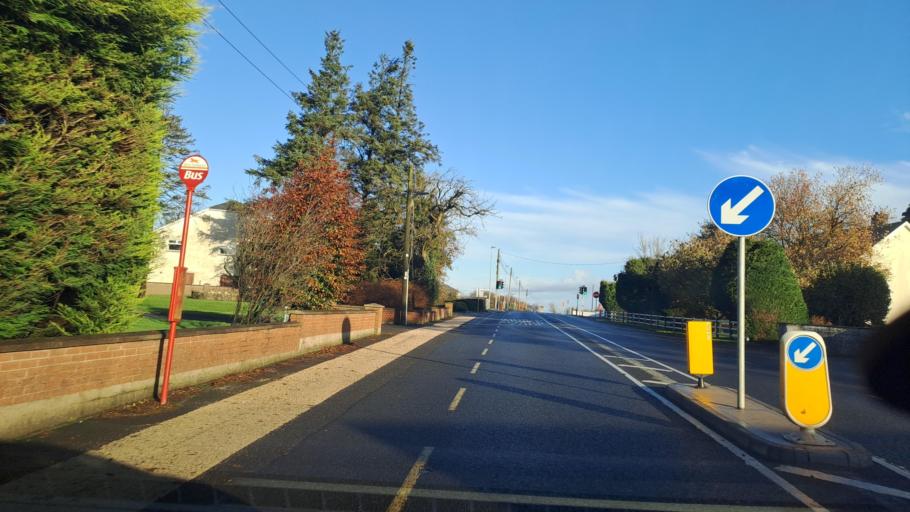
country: IE
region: Ulster
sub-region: County Monaghan
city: Monaghan
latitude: 54.1900
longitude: -6.9903
